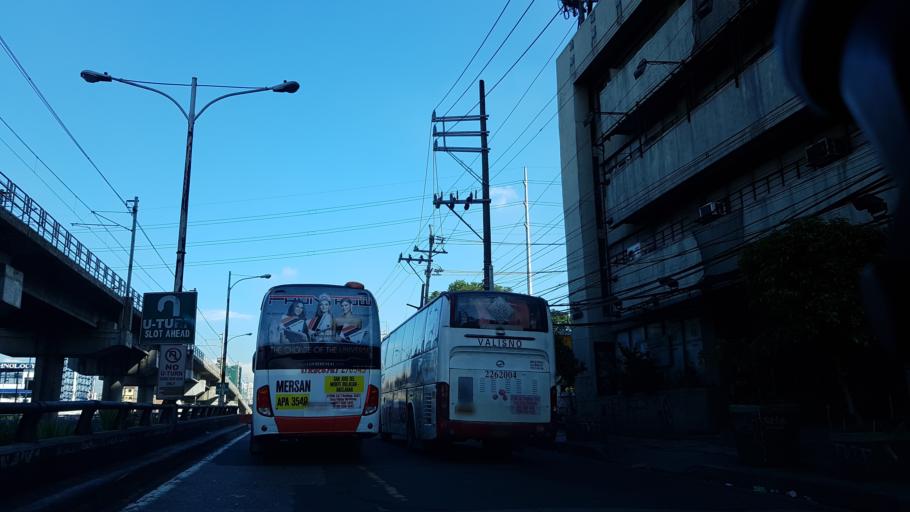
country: PH
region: Metro Manila
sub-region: San Juan
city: San Juan
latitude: 14.6157
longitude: 121.0530
